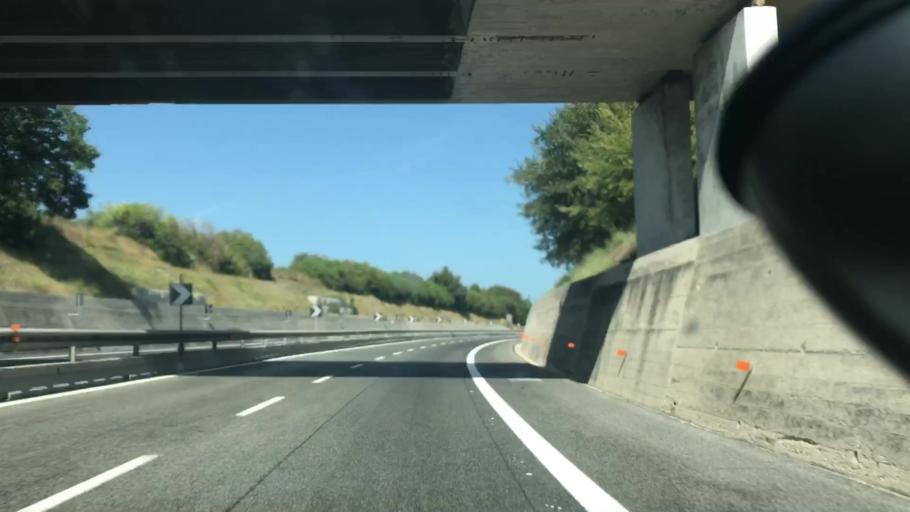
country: IT
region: Abruzzo
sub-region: Provincia di Chieti
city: San Vito Chietino
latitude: 42.3027
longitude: 14.4228
